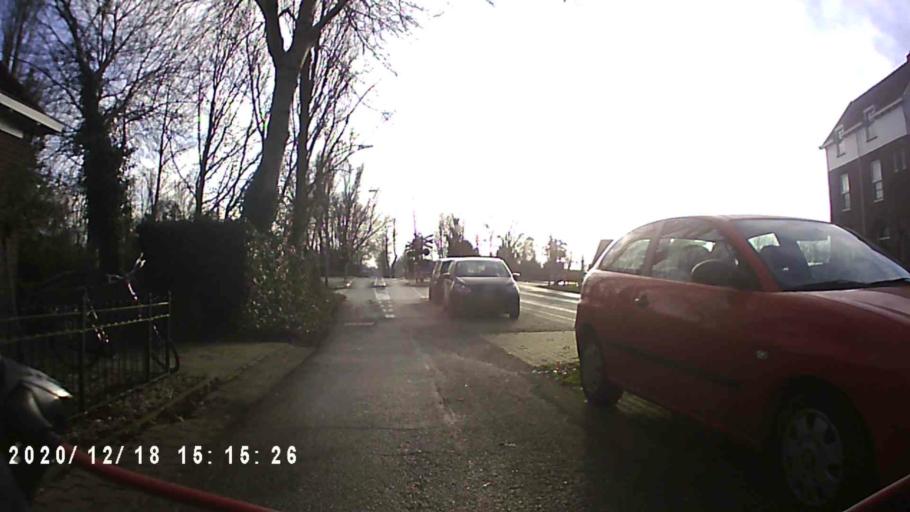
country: NL
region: Groningen
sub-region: Gemeente Hoogezand-Sappemeer
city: Hoogezand
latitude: 53.1620
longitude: 6.7222
